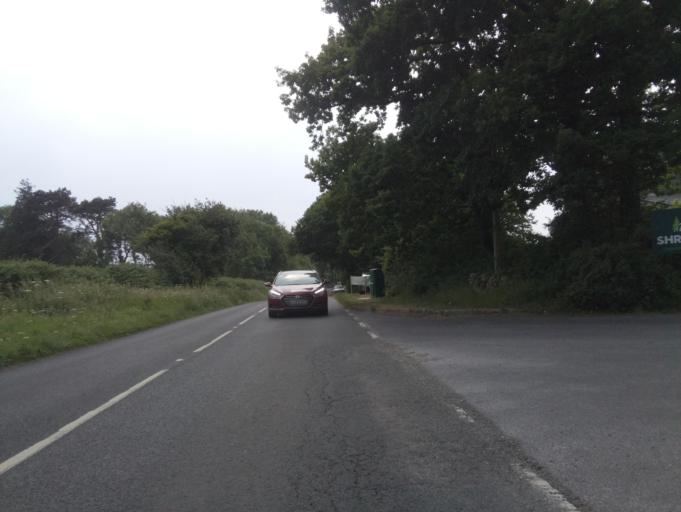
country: GB
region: England
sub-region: Dorset
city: Lyme Regis
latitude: 50.7167
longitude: -2.9952
